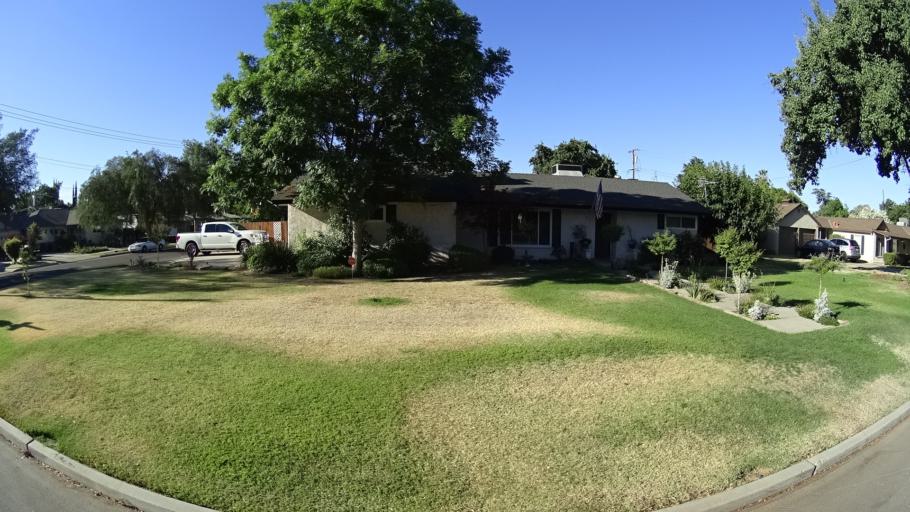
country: US
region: California
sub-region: Fresno County
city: Fresno
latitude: 36.8019
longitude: -119.8223
